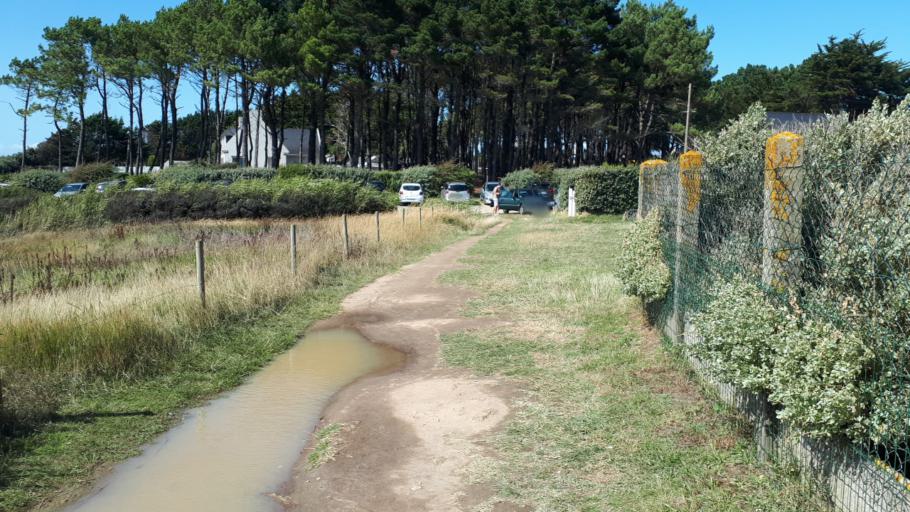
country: FR
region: Brittany
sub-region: Departement du Morbihan
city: Penestin
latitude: 47.4496
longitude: -2.4932
